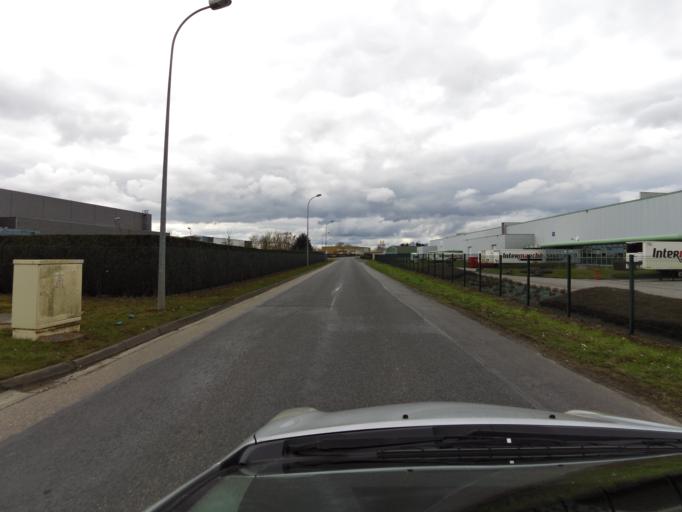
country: FR
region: Picardie
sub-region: Departement de la Somme
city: Chaulnes
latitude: 49.8047
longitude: 2.8021
